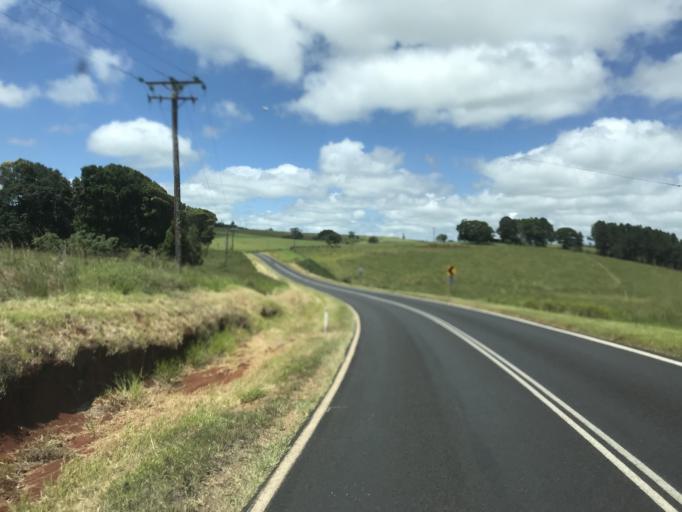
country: AU
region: Queensland
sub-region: Tablelands
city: Ravenshoe
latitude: -17.5086
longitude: 145.4746
